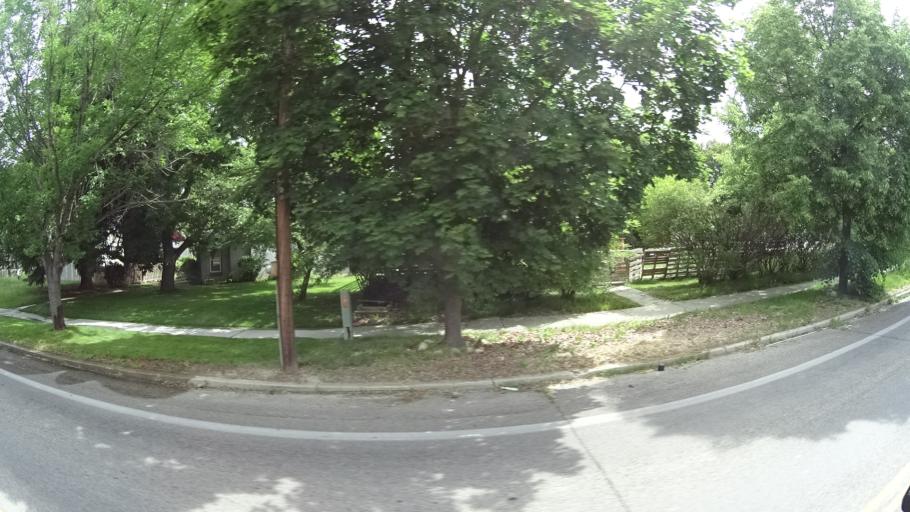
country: US
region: Idaho
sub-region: Ada County
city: Boise
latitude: 43.5924
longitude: -116.1967
